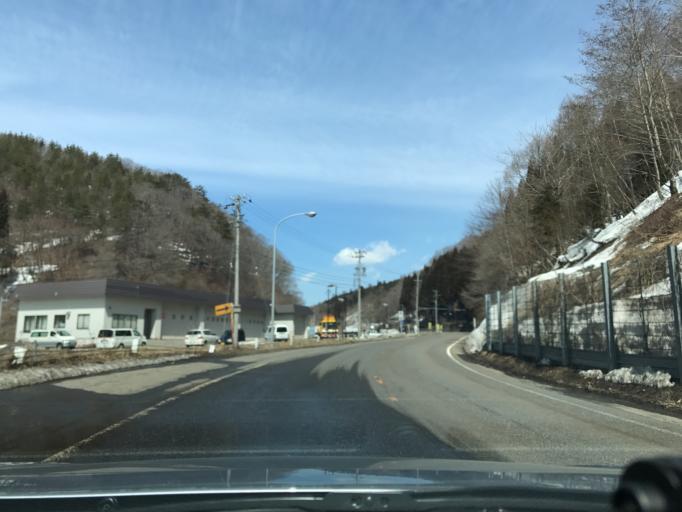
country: JP
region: Nagano
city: Omachi
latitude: 36.5809
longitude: 137.8393
